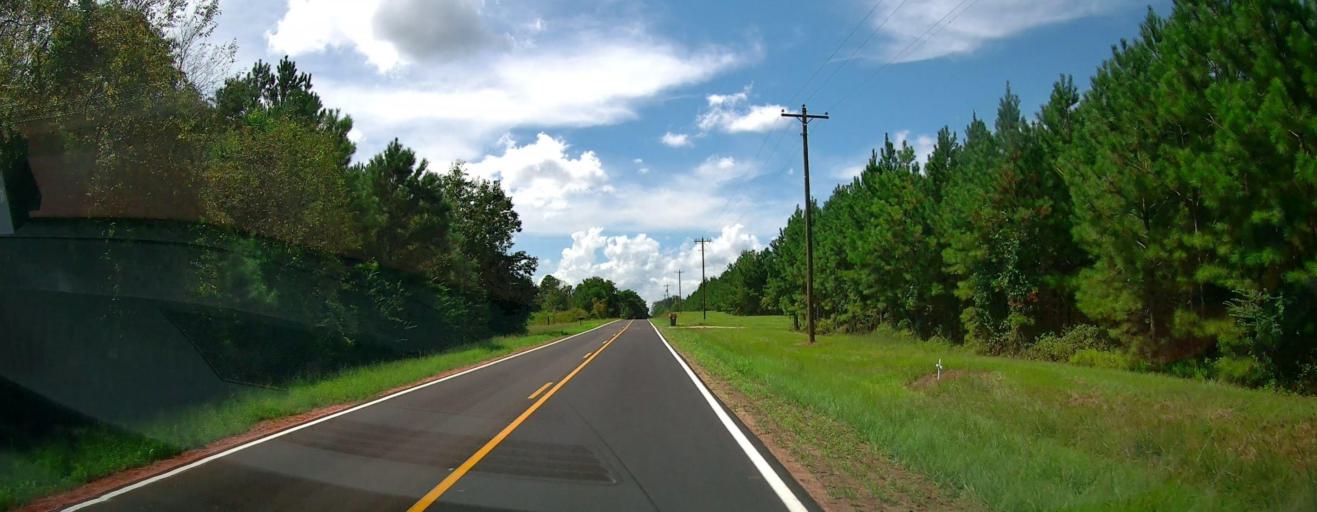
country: US
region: Georgia
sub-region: Macon County
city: Marshallville
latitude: 32.4725
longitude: -83.8713
